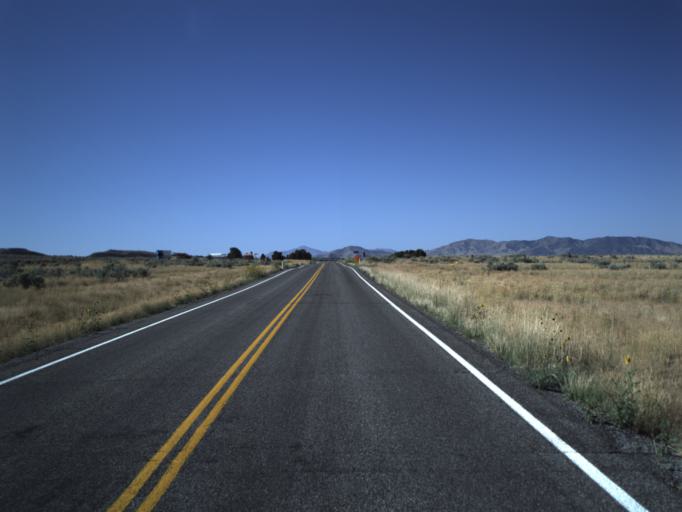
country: US
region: Utah
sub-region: Juab County
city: Mona
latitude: 39.8089
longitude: -112.1436
